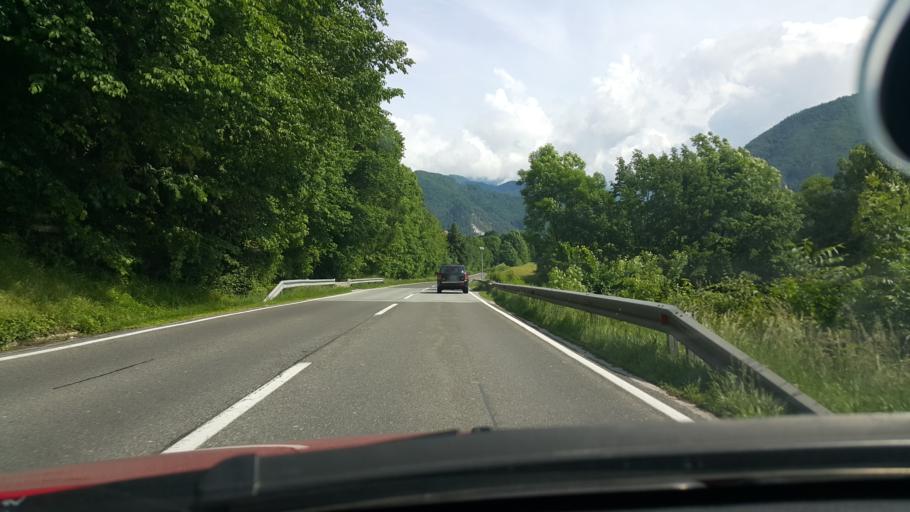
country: SI
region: Trzic
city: Bistrica pri Trzicu
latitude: 46.3356
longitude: 14.2825
